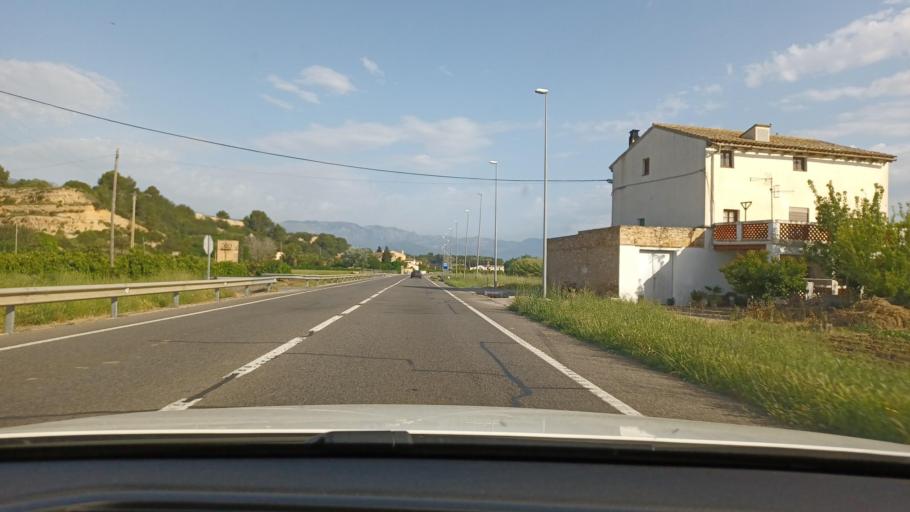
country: ES
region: Catalonia
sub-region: Provincia de Tarragona
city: Tortosa
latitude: 40.7779
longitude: 0.5077
